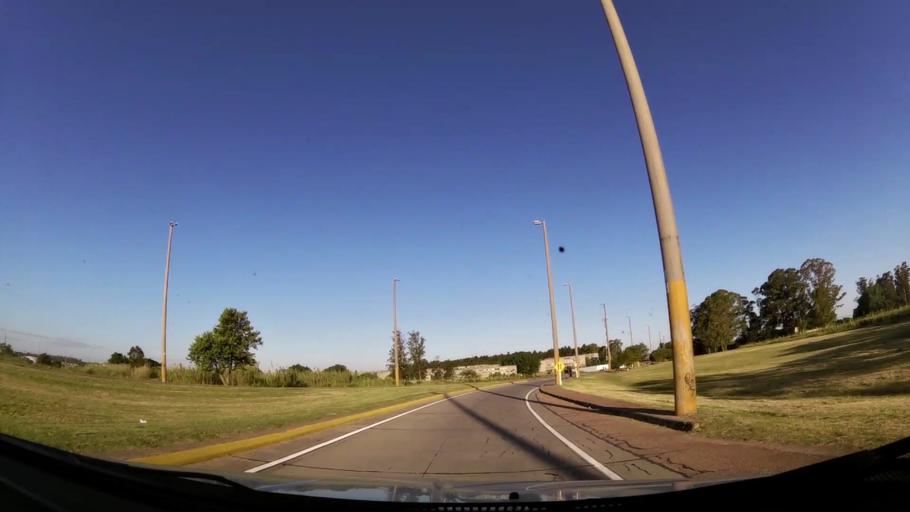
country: UY
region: Canelones
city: La Paz
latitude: -34.8263
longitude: -56.2456
